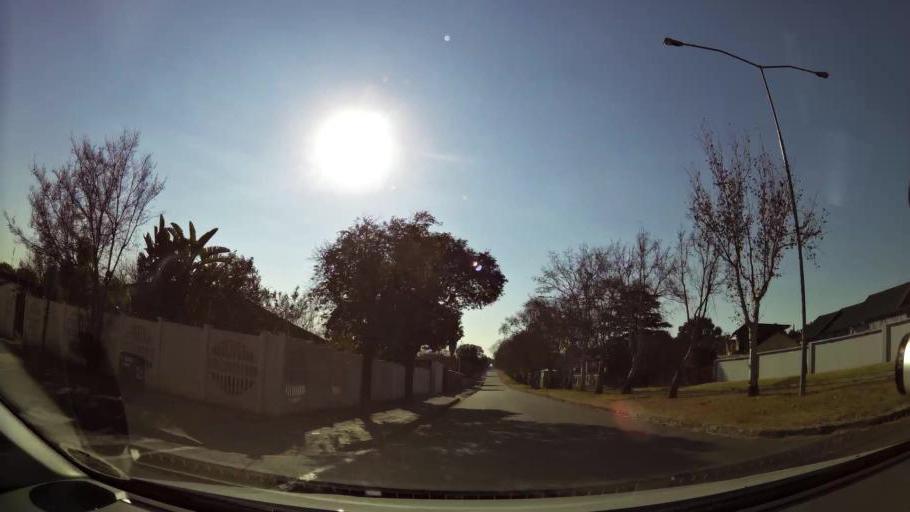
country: ZA
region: Gauteng
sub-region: City of Johannesburg Metropolitan Municipality
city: Modderfontein
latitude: -26.1428
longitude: 28.1487
